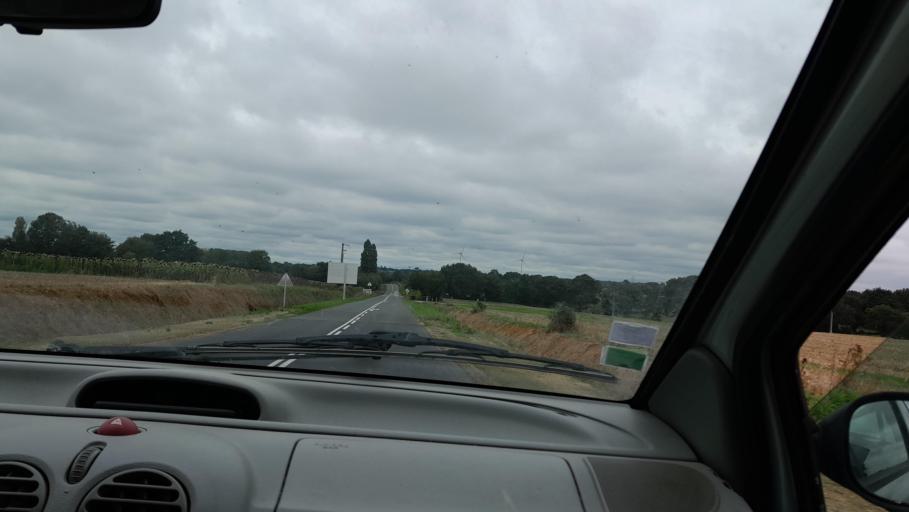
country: FR
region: Pays de la Loire
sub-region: Departement de la Mayenne
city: Cosse-le-Vivien
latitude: 47.9523
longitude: -0.9296
